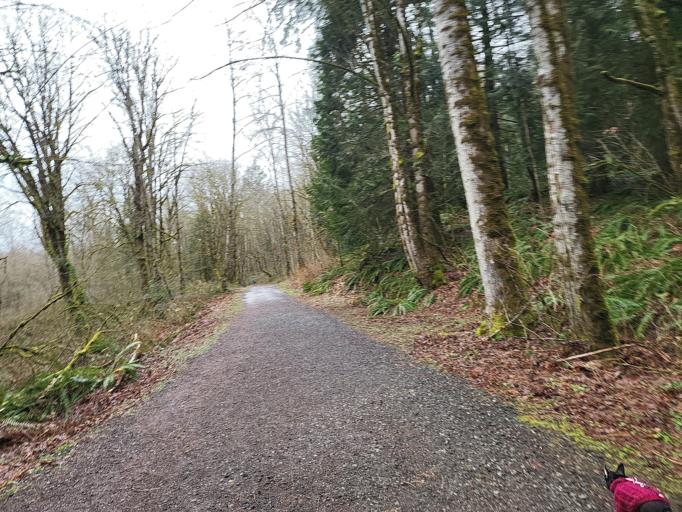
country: US
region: Washington
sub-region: King County
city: Newcastle
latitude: 47.5296
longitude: -122.1228
